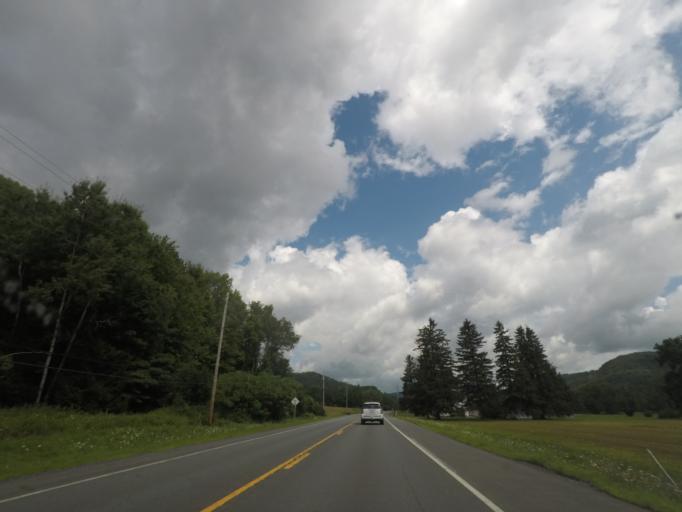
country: US
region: Massachusetts
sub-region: Berkshire County
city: Williamstown
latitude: 42.6649
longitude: -73.3704
